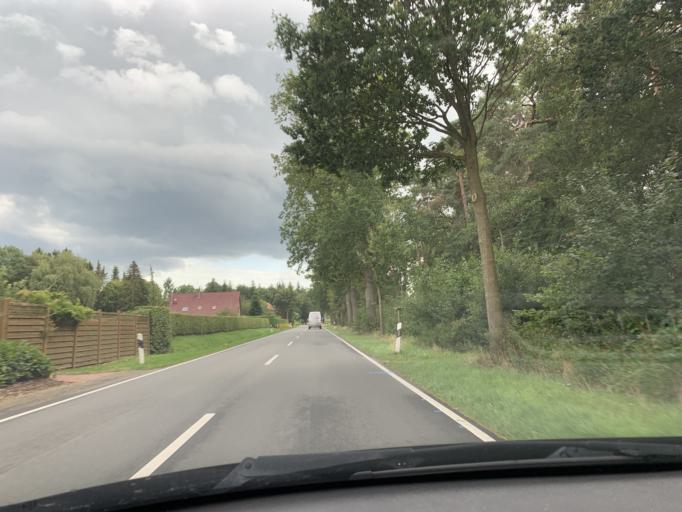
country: DE
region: Lower Saxony
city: Westerstede
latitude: 53.2932
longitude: 7.9210
